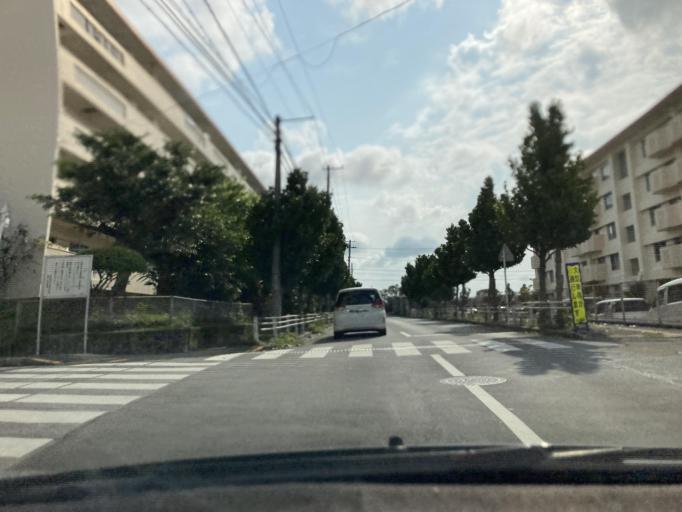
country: JP
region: Okinawa
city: Tomigusuku
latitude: 26.1986
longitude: 127.7204
